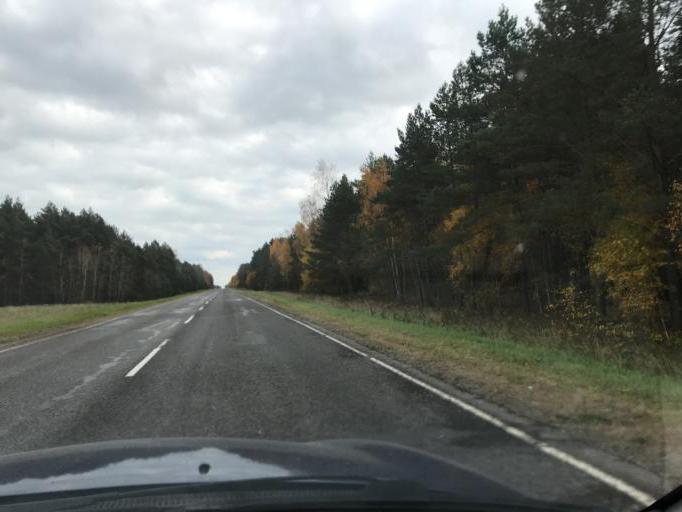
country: BY
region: Grodnenskaya
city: Lida
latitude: 53.7462
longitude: 25.2981
